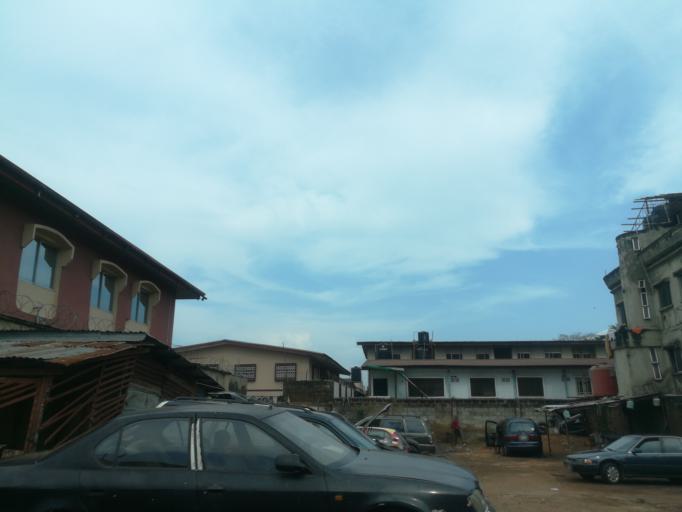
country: NG
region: Oyo
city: Ibadan
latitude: 7.4136
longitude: 3.8967
